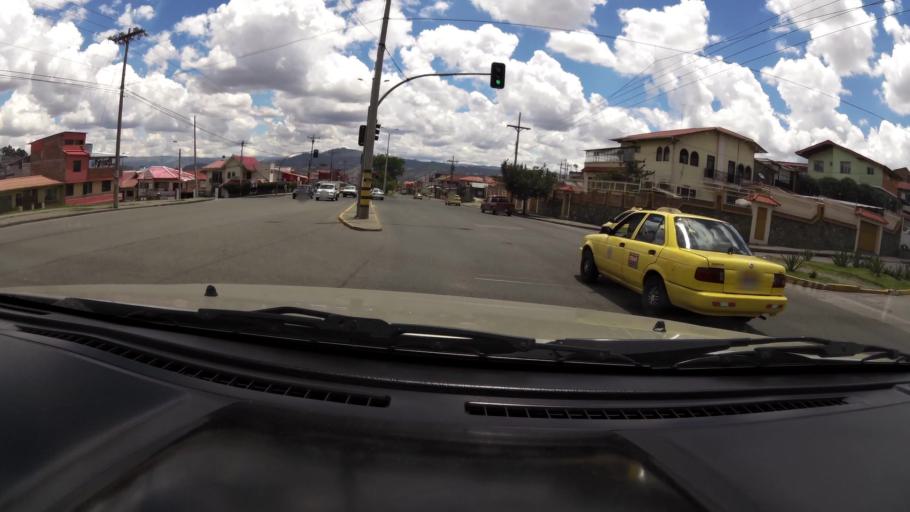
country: EC
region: Azuay
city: Cuenca
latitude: -2.8856
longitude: -78.9989
